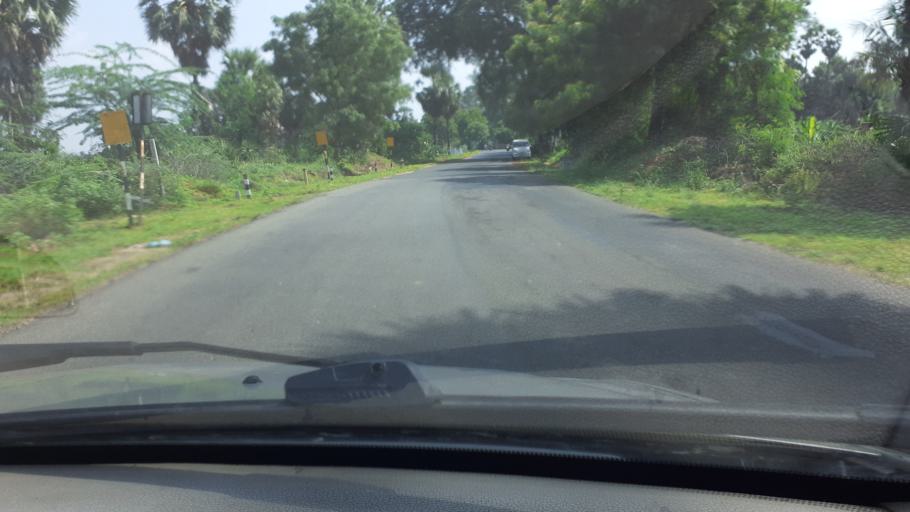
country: IN
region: Tamil Nadu
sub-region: Thoothukkudi
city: Srivaikuntam
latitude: 8.6332
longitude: 77.8885
